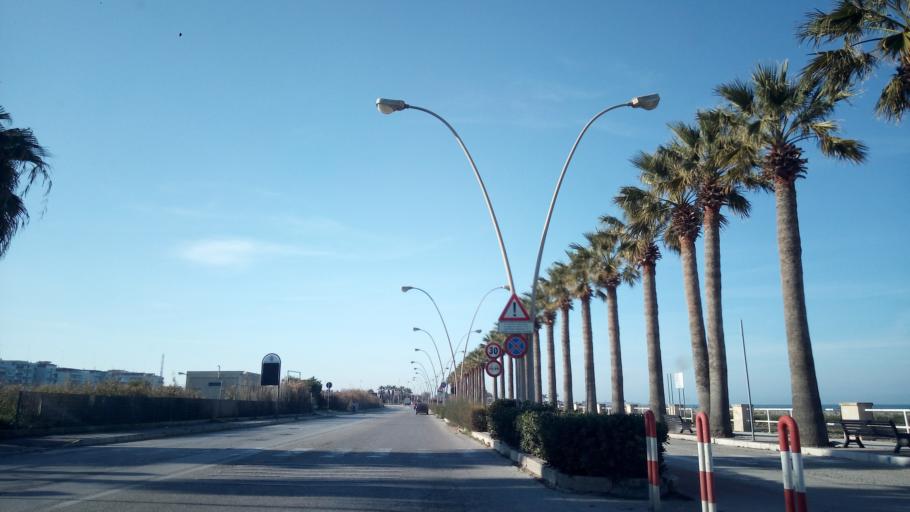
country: IT
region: Apulia
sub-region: Provincia di Barletta - Andria - Trani
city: Barletta
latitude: 41.3247
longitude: 16.2707
